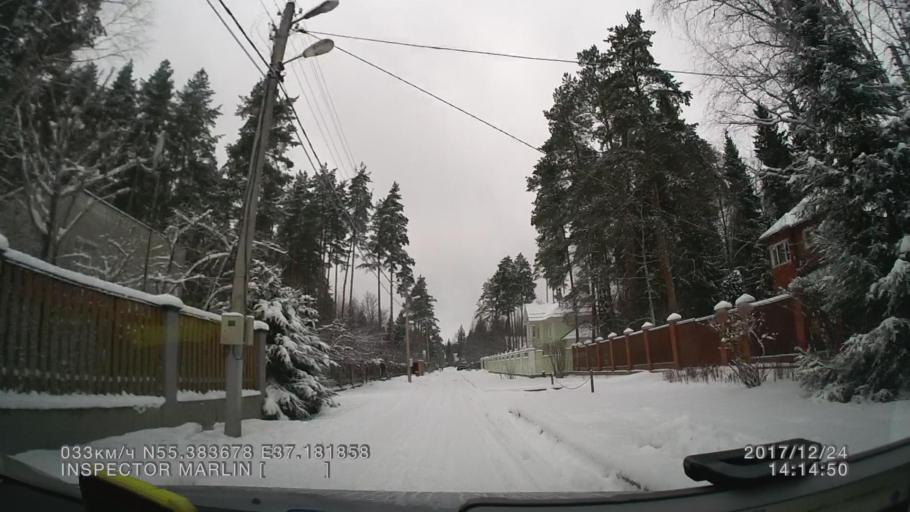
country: RU
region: Moskovskaya
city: Troitsk
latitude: 55.3837
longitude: 37.1818
